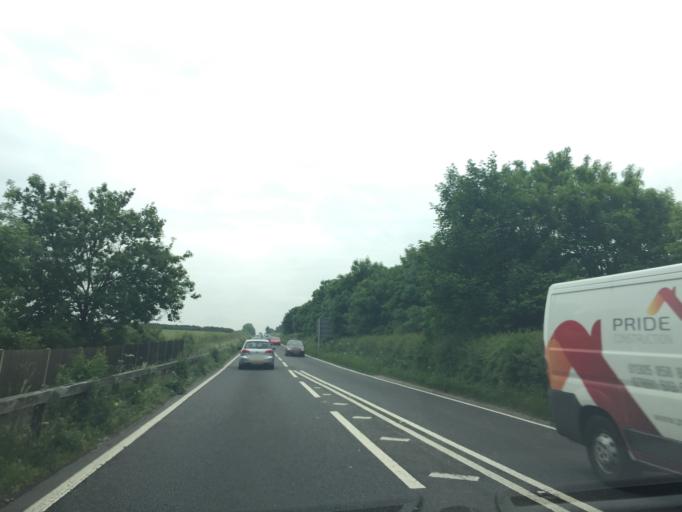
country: GB
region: England
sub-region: Dorset
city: Dorchester
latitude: 50.6900
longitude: -2.4547
